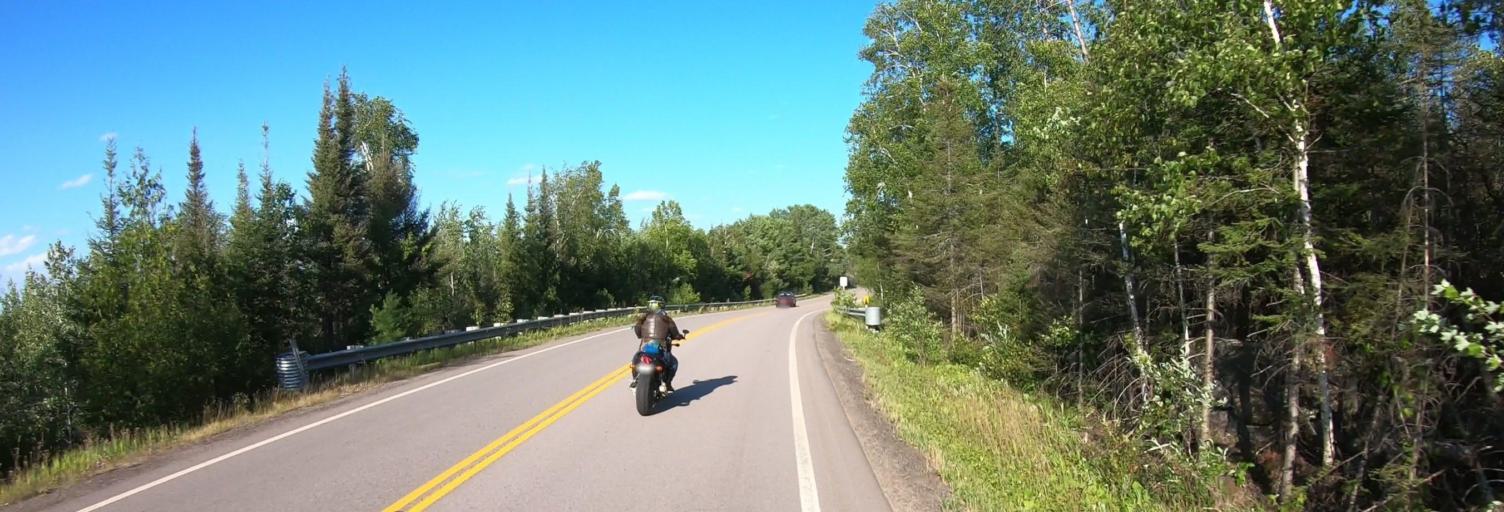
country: US
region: Minnesota
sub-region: Saint Louis County
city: Ely
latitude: 47.9619
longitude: -91.5420
